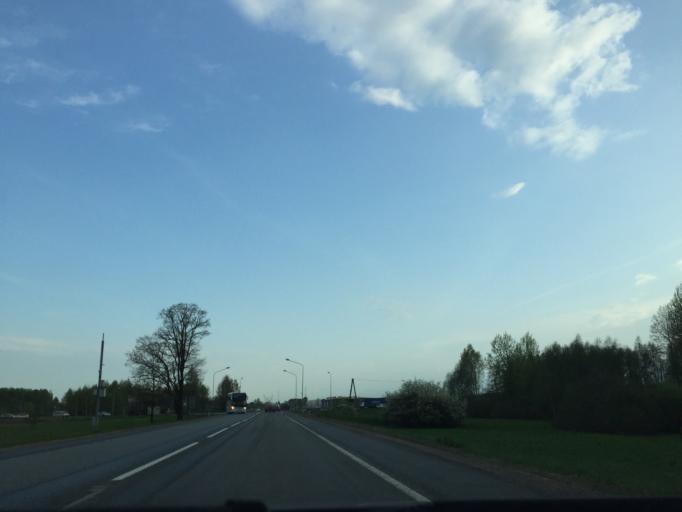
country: LV
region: Kekava
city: Kekava
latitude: 56.8143
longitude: 24.2465
